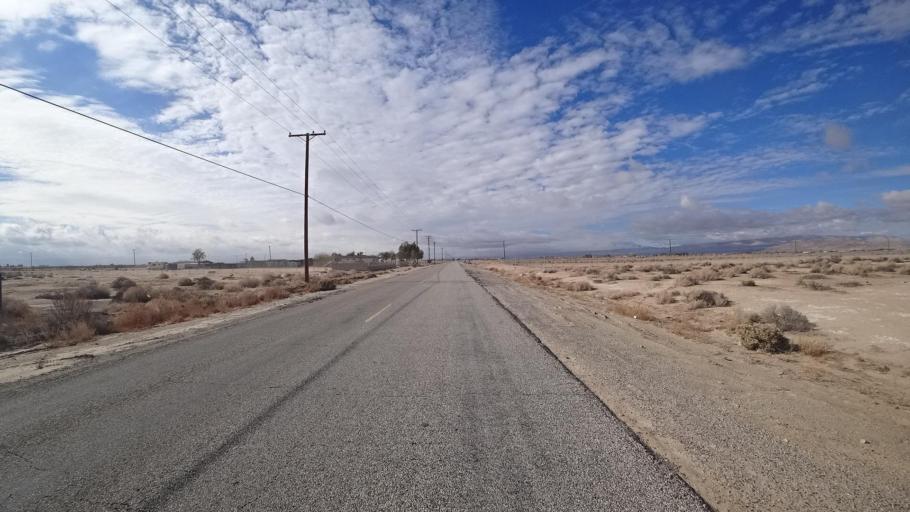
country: US
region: California
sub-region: Kern County
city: Rosamond
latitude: 34.8202
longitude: -118.2177
